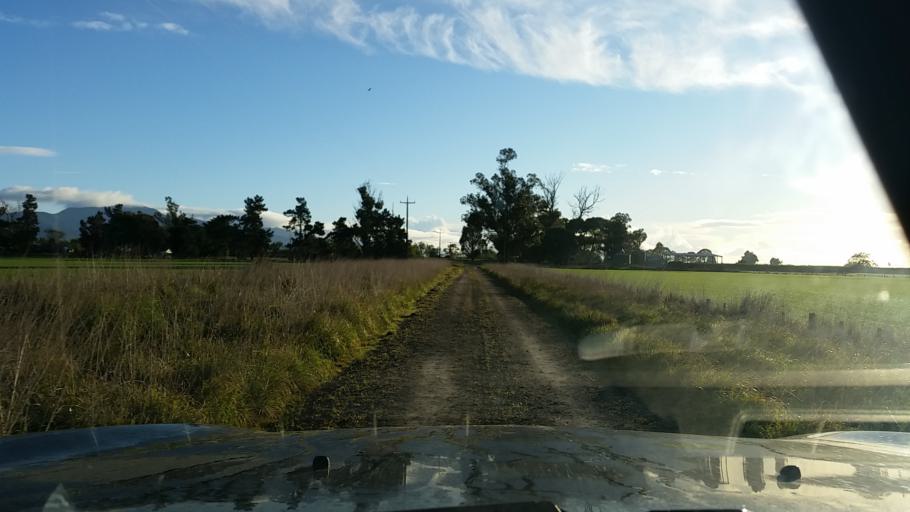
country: NZ
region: Marlborough
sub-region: Marlborough District
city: Blenheim
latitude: -41.5022
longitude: 174.0328
